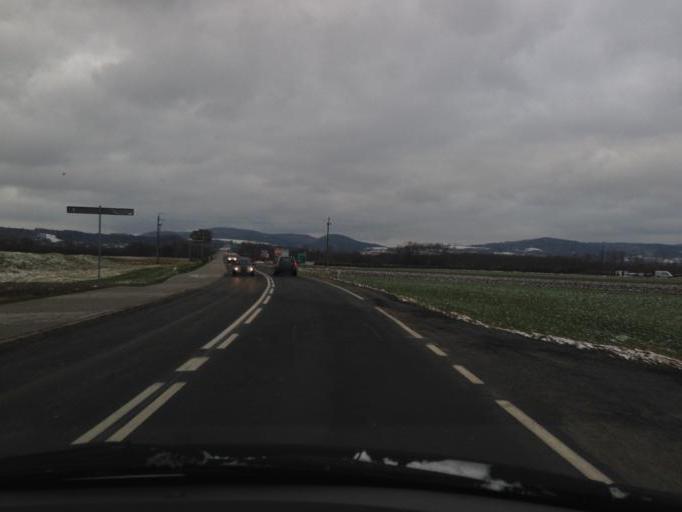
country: PL
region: Lesser Poland Voivodeship
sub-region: Powiat tarnowski
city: Zakliczyn
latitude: 49.8717
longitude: 20.8108
